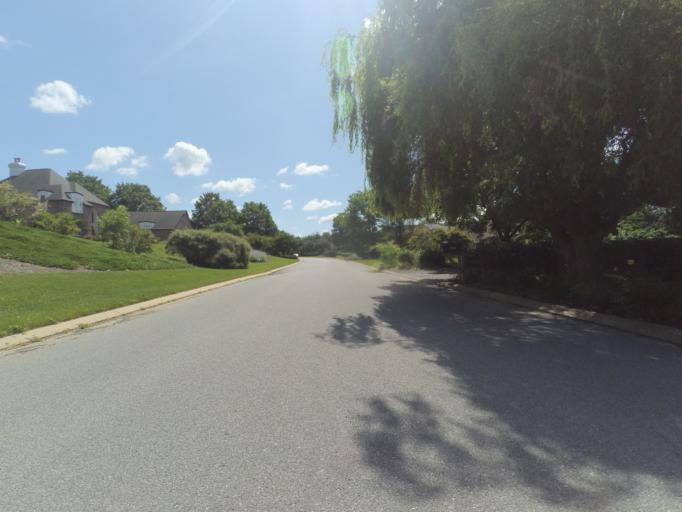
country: US
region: Pennsylvania
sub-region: Centre County
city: Lemont
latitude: 40.7923
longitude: -77.8285
